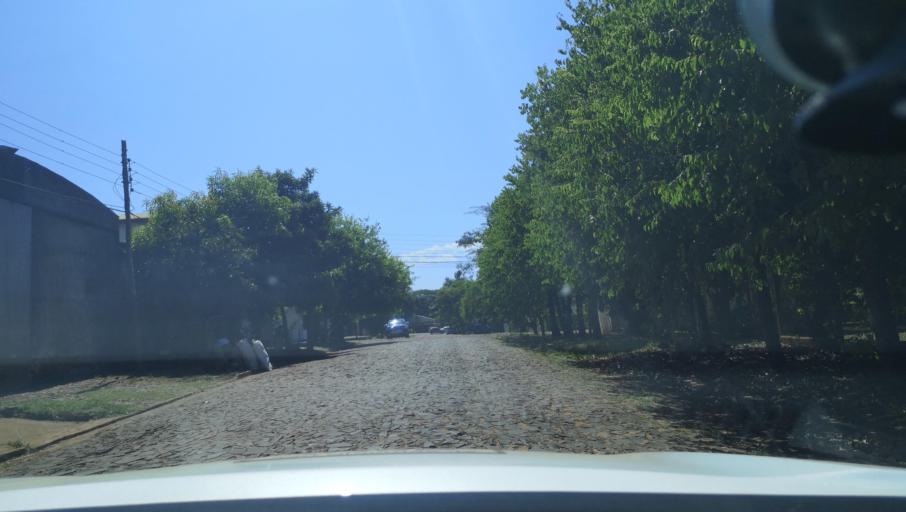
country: PY
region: Itapua
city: Carmen del Parana
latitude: -27.1587
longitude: -56.2325
